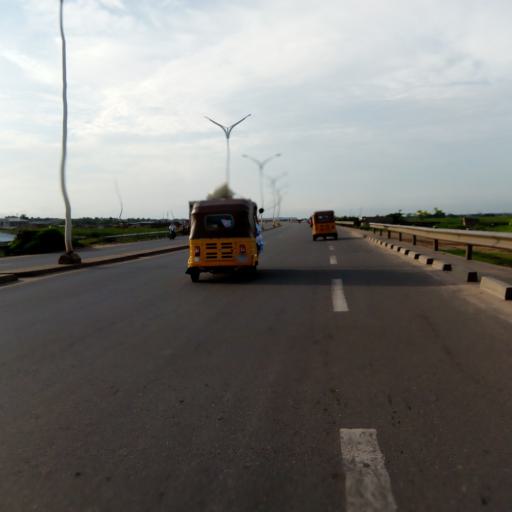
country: TG
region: Maritime
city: Lome
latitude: 6.1838
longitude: 1.2795
